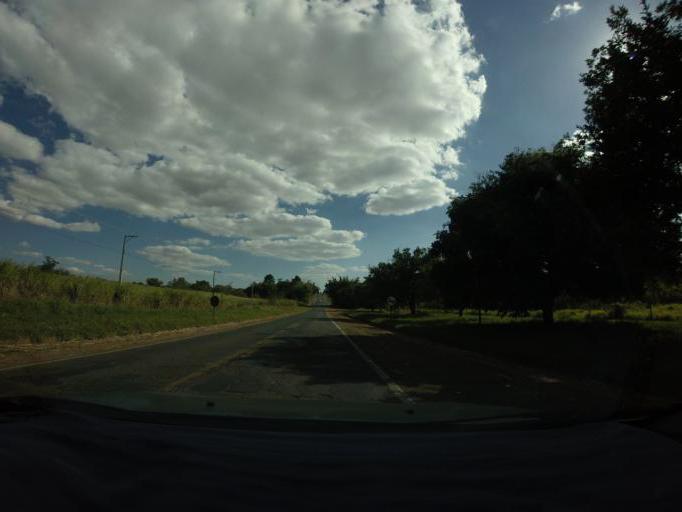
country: BR
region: Sao Paulo
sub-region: Piracicaba
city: Piracicaba
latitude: -22.7348
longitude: -47.5561
